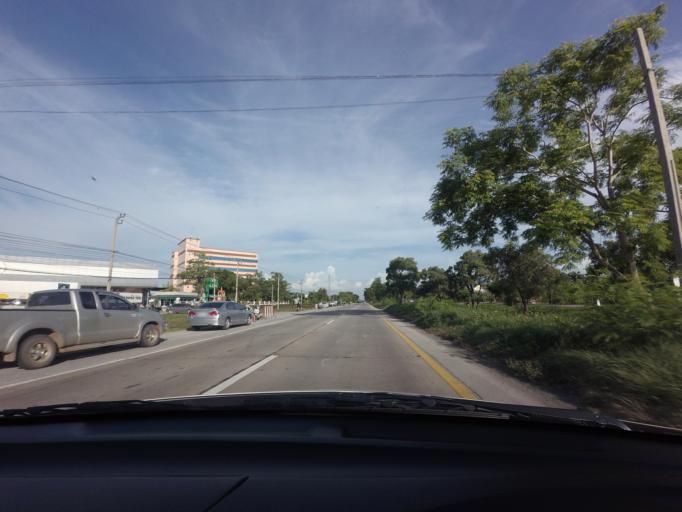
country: TH
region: Phra Nakhon Si Ayutthaya
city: Lat Bua Luang
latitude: 14.0762
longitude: 100.3182
